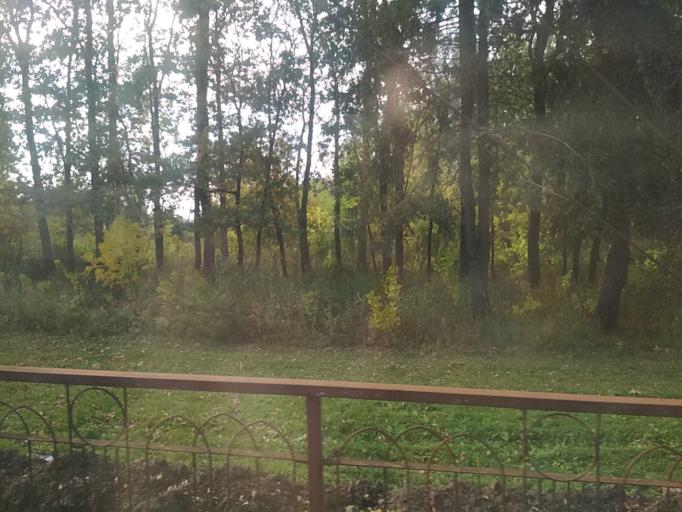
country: BY
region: Minsk
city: Syenitsa
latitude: 53.8191
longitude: 27.5727
